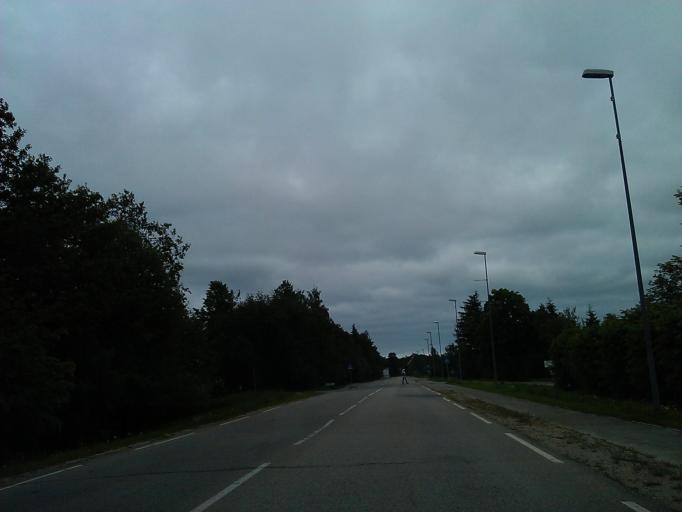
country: LV
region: Carnikava
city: Carnikava
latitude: 57.1273
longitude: 24.2902
